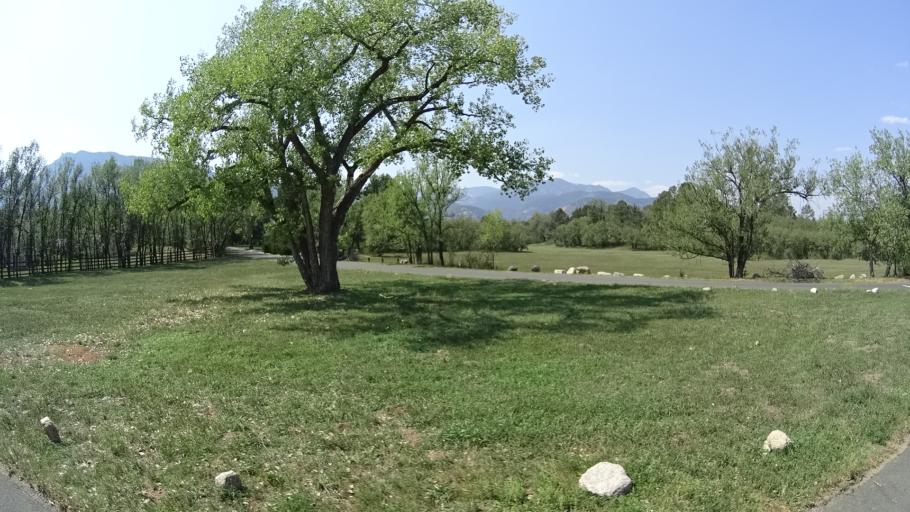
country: US
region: Colorado
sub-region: El Paso County
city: Colorado Springs
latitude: 38.7854
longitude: -104.8375
